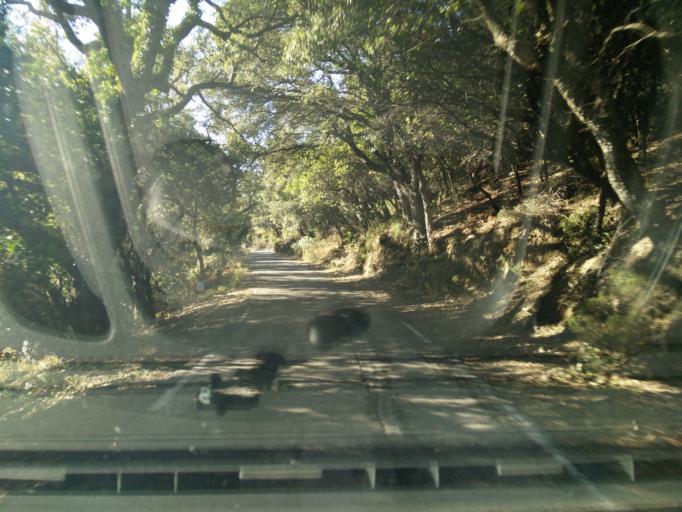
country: FR
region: Provence-Alpes-Cote d'Azur
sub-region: Departement du Var
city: La Garde-Freinet
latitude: 43.2541
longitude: 6.4067
